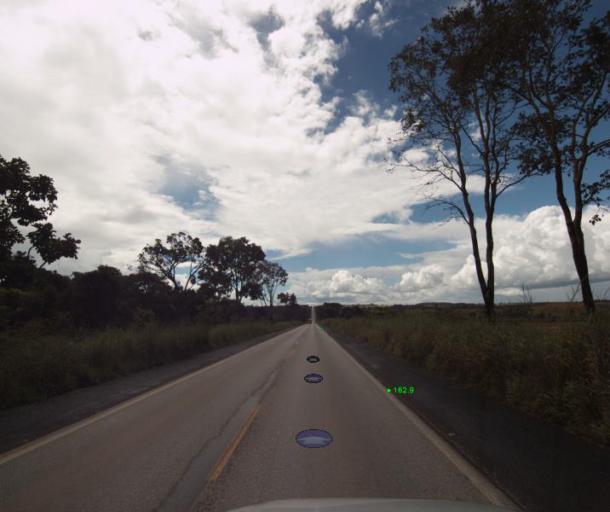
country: BR
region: Goias
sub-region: Uruacu
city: Uruacu
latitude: -14.1985
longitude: -49.1288
